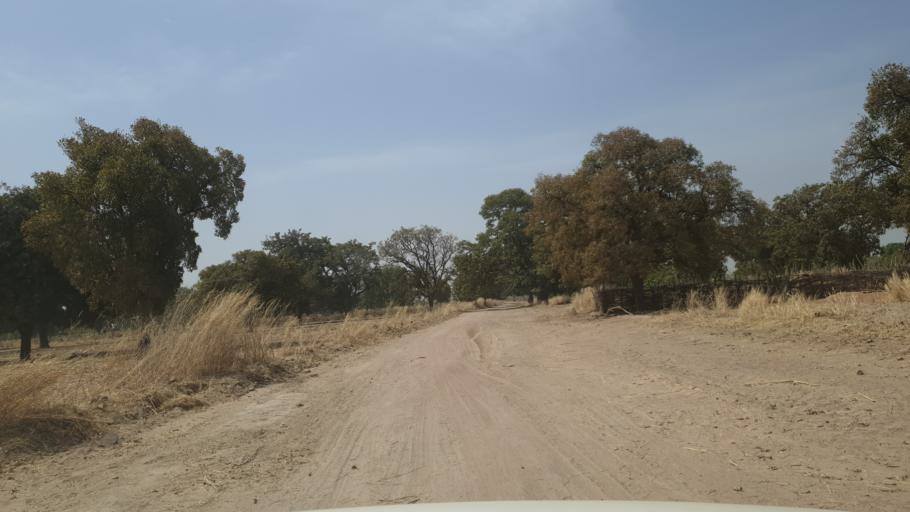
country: ML
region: Koulikoro
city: Kolokani
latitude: 13.4758
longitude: -8.1857
